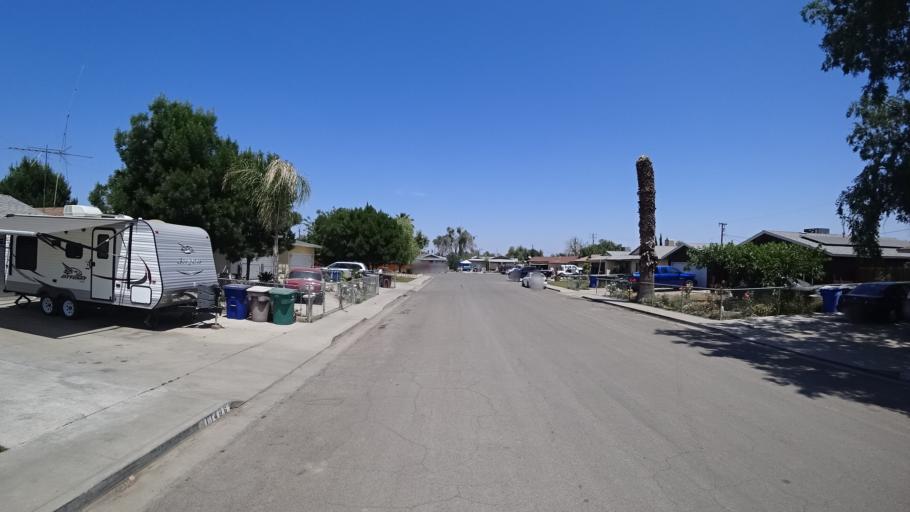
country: US
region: California
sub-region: Kings County
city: Armona
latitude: 36.3060
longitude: -119.7124
